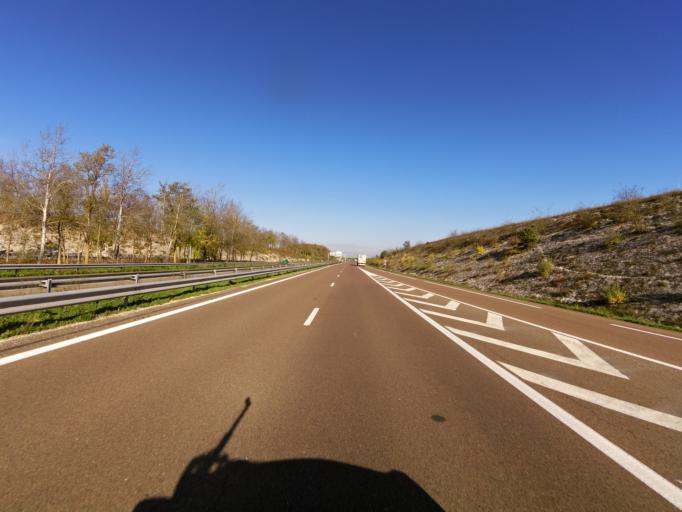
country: FR
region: Champagne-Ardenne
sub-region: Departement de la Marne
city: Fagnieres
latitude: 48.9081
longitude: 4.2841
